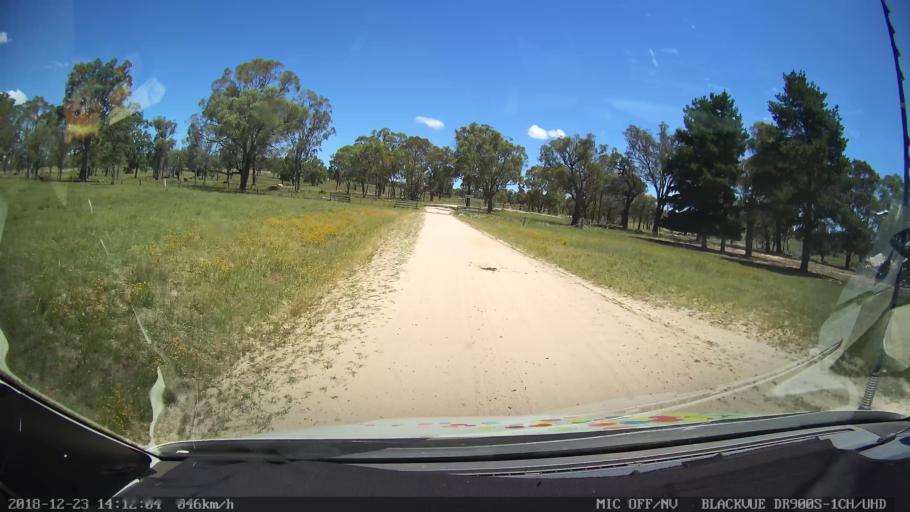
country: AU
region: New South Wales
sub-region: Tamworth Municipality
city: Manilla
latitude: -30.6537
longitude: 151.0468
